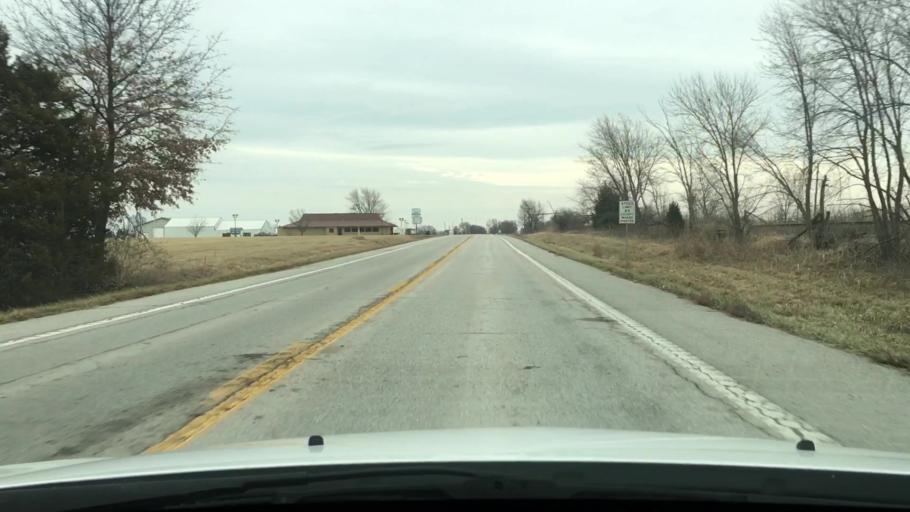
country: US
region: Missouri
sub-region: Audrain County
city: Vandalia
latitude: 39.3007
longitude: -91.5087
